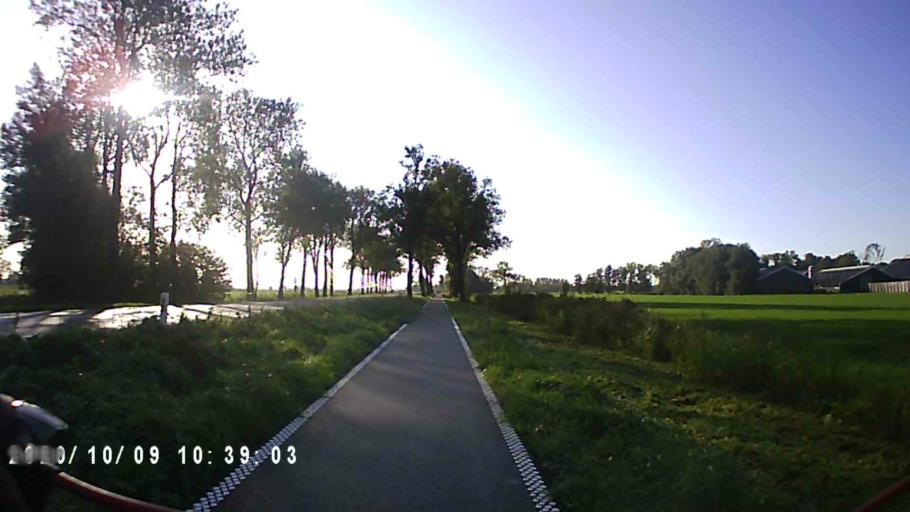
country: NL
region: Groningen
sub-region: Gemeente Winsum
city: Winsum
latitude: 53.2861
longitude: 6.5335
